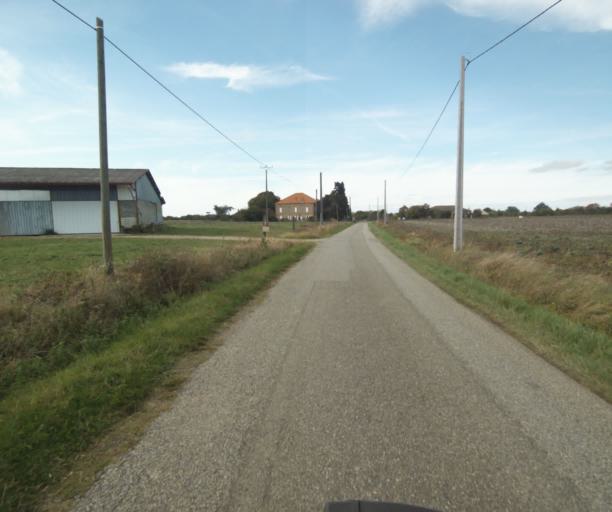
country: FR
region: Midi-Pyrenees
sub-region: Departement du Tarn-et-Garonne
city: Saint-Porquier
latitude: 43.9515
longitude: 1.1546
